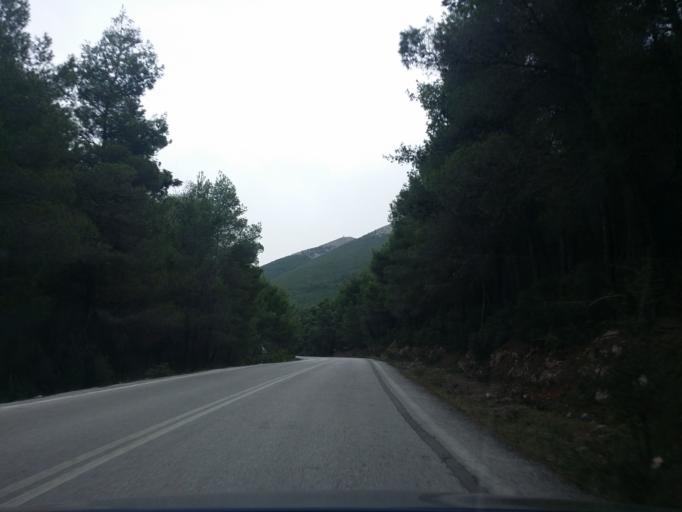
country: GR
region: Attica
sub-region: Nomarchia Dytikis Attikis
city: Vilia
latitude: 38.1439
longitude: 23.2835
